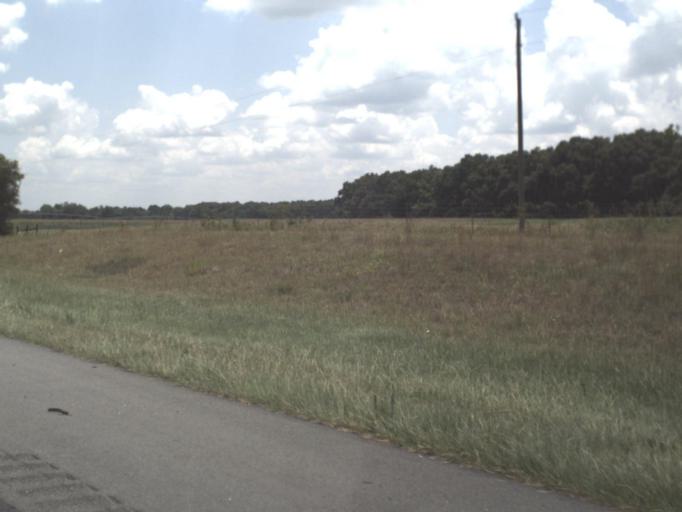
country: US
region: Florida
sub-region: Hamilton County
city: Jasper
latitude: 30.5364
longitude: -83.0716
